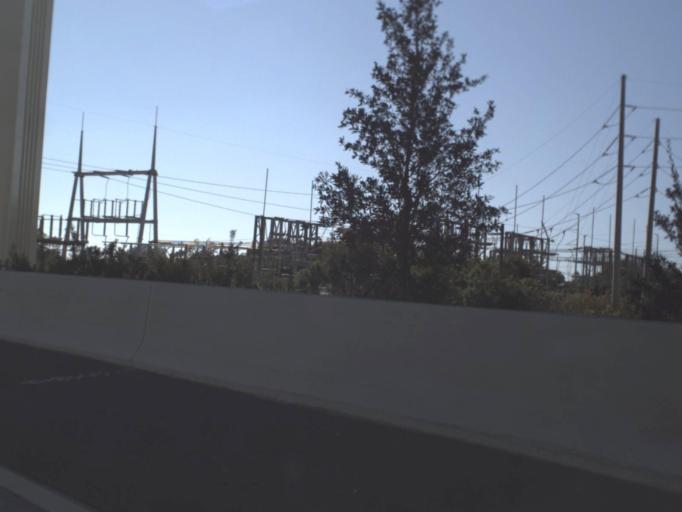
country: US
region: Florida
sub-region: Hillsborough County
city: Tampa
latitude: 27.9642
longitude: -82.4259
